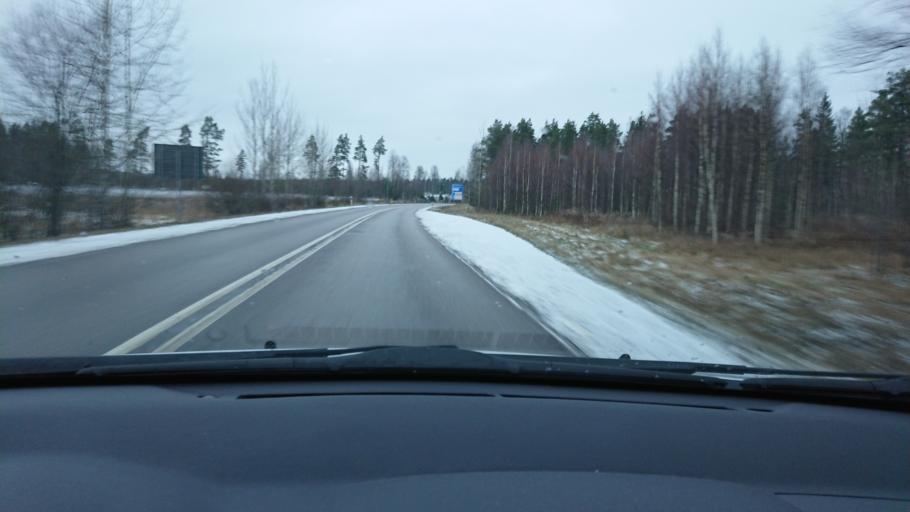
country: SE
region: Kalmar
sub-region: Hultsfreds Kommun
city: Hultsfred
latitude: 57.4970
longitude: 15.8209
